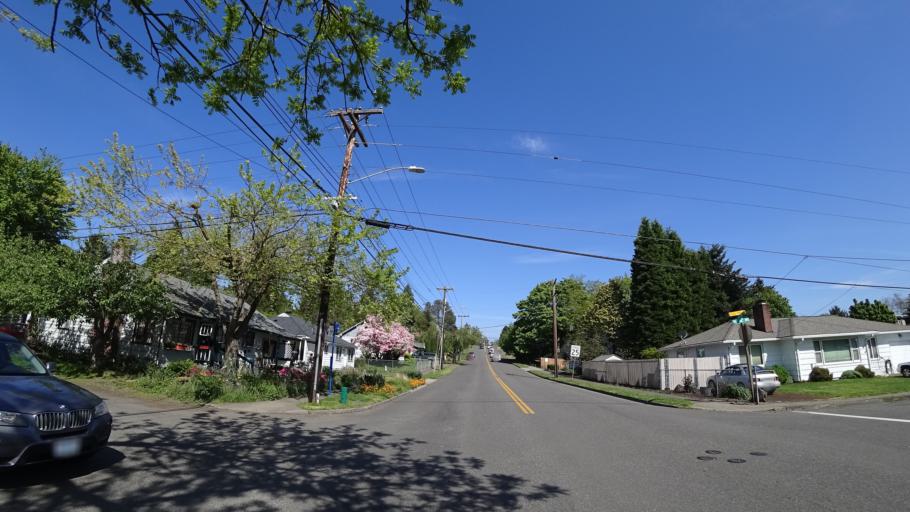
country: US
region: Oregon
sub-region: Clackamas County
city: Milwaukie
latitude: 45.4467
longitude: -122.6276
